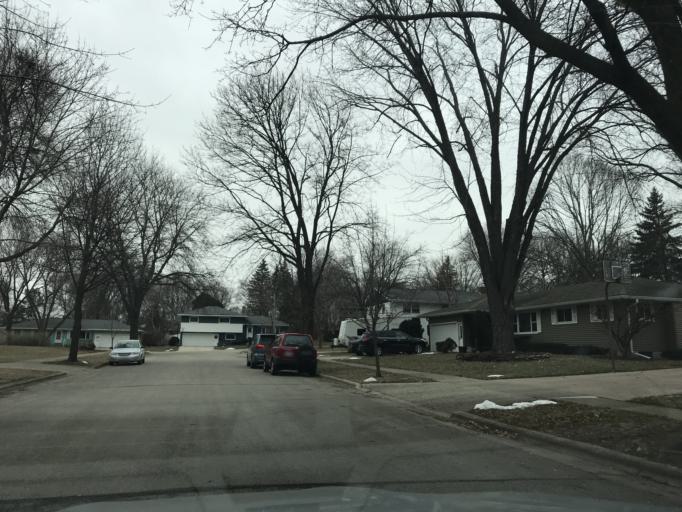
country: US
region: Wisconsin
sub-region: Dane County
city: Monona
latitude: 43.0912
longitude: -89.2998
